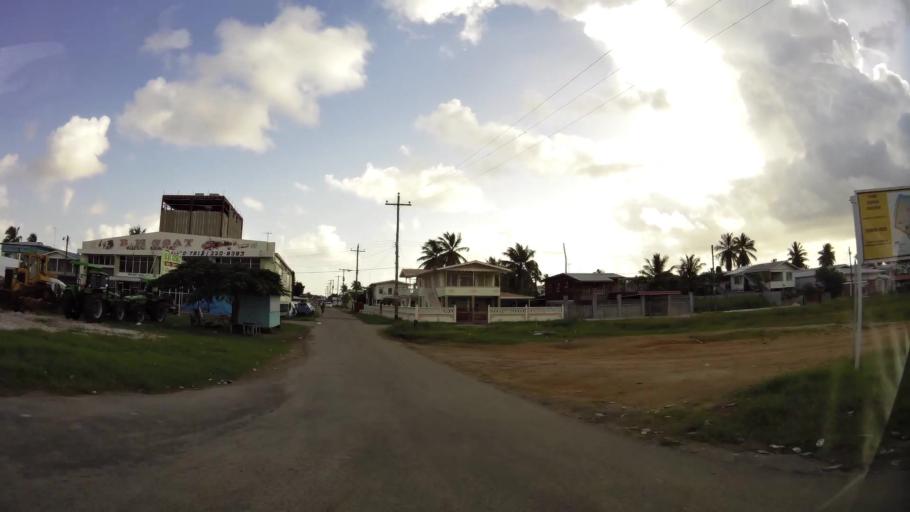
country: GY
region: Demerara-Mahaica
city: Georgetown
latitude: 6.7991
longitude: -58.0398
